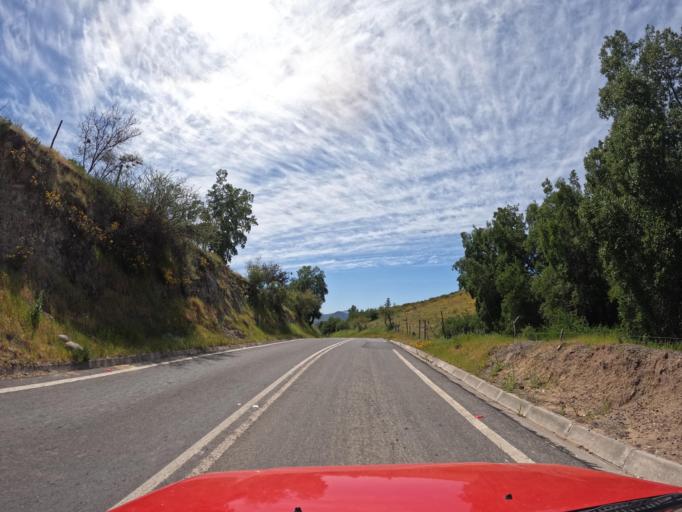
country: CL
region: Maule
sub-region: Provincia de Talca
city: Talca
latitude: -35.0649
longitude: -71.7351
